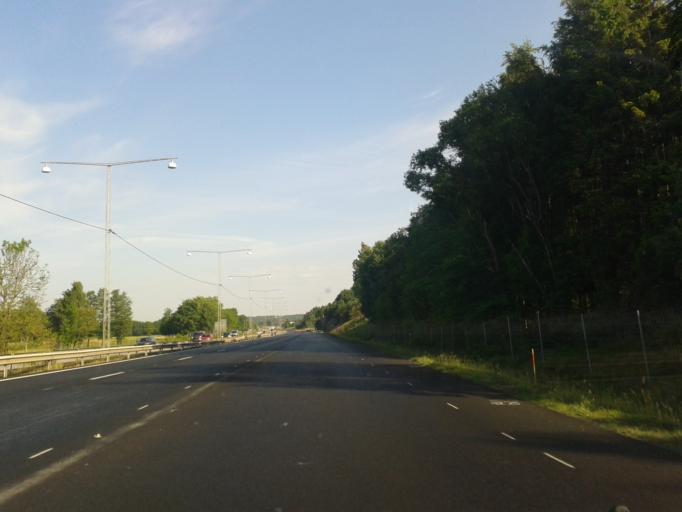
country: SE
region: Vaestra Goetaland
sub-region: Kungalvs Kommun
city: Kungalv
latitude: 57.8866
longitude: 11.9430
